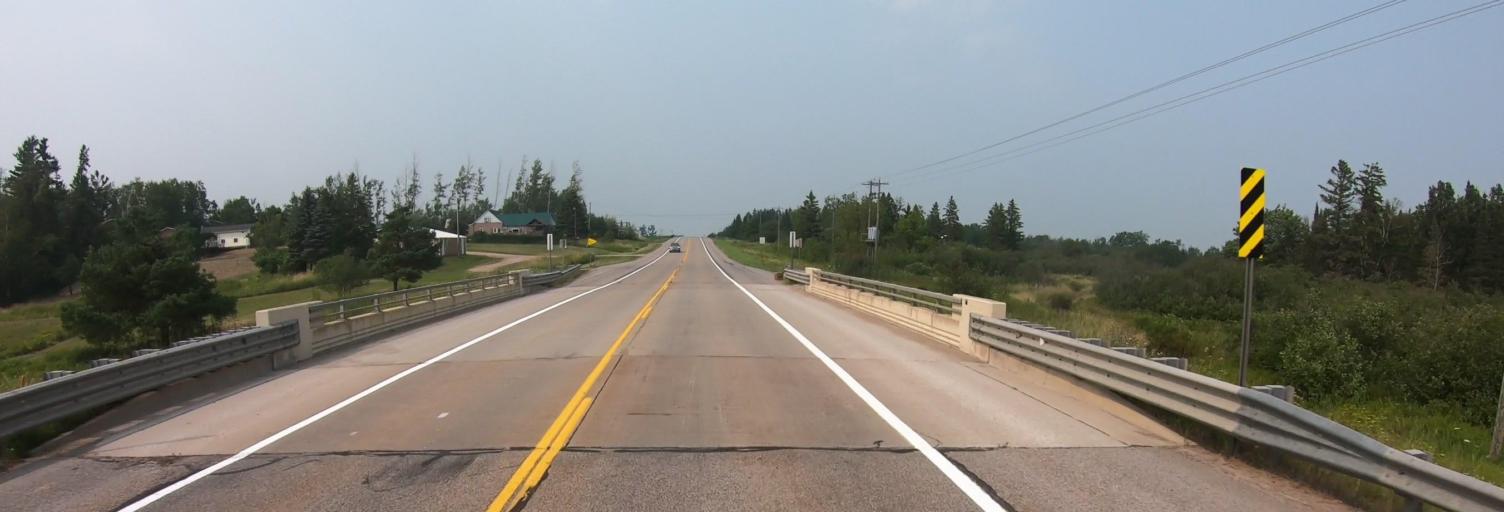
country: US
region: Michigan
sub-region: Chippewa County
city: Sault Ste. Marie
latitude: 46.3340
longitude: -84.3639
